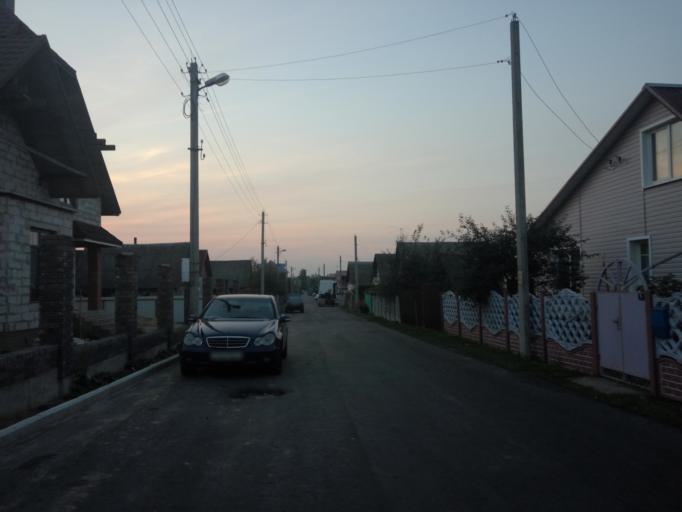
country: BY
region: Vitebsk
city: Vitebsk
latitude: 55.2026
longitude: 30.2475
